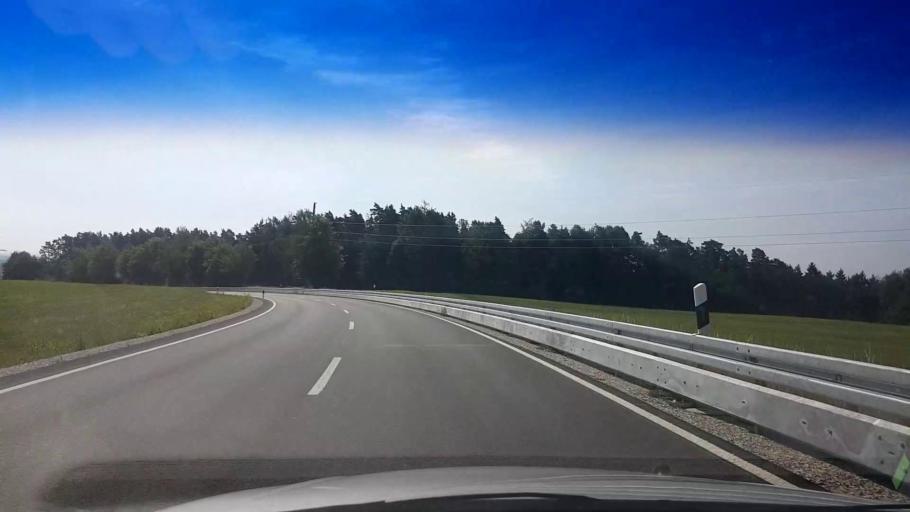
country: DE
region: Bavaria
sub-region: Upper Franconia
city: Mistelgau
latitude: 49.9401
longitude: 11.4512
